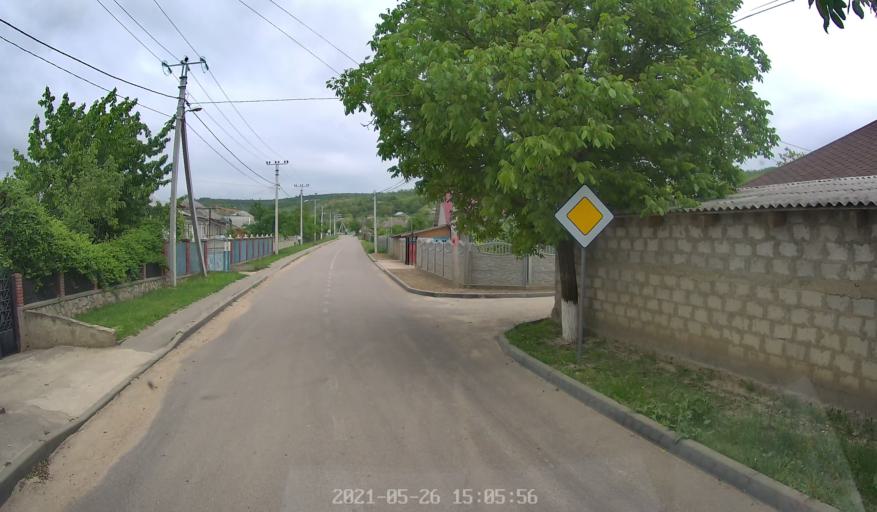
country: MD
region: Hincesti
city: Dancu
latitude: 46.6640
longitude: 28.3309
